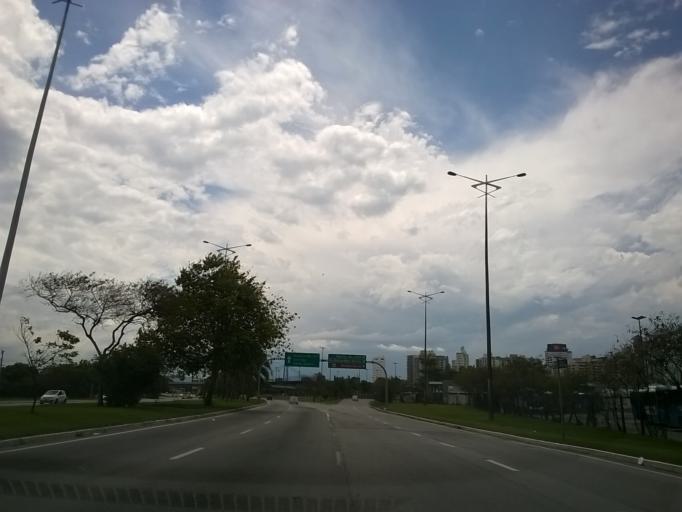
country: BR
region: Santa Catarina
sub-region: Florianopolis
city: Florianopolis
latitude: -27.6002
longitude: -48.5529
